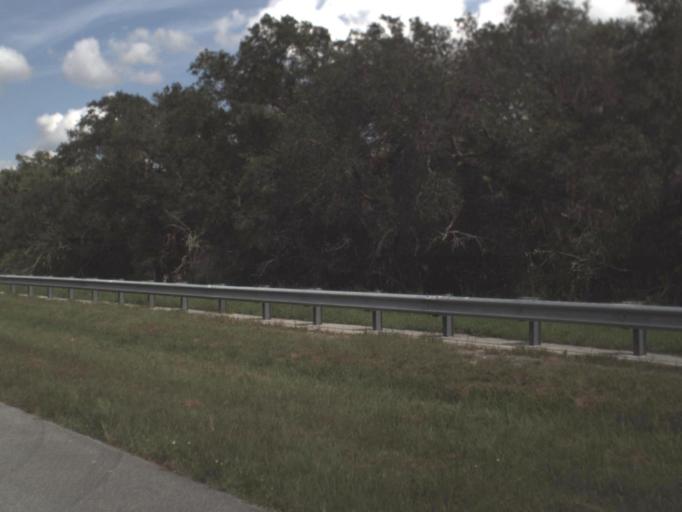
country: US
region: Florida
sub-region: Collier County
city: Lely Resort
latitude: 25.9896
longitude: -81.3475
